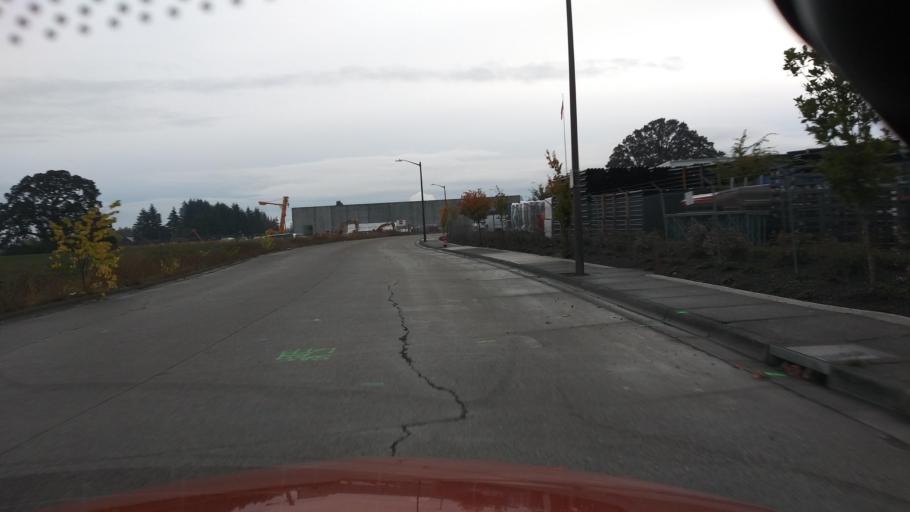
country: US
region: Oregon
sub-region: Washington County
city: Cornelius
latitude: 45.5267
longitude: -123.0656
